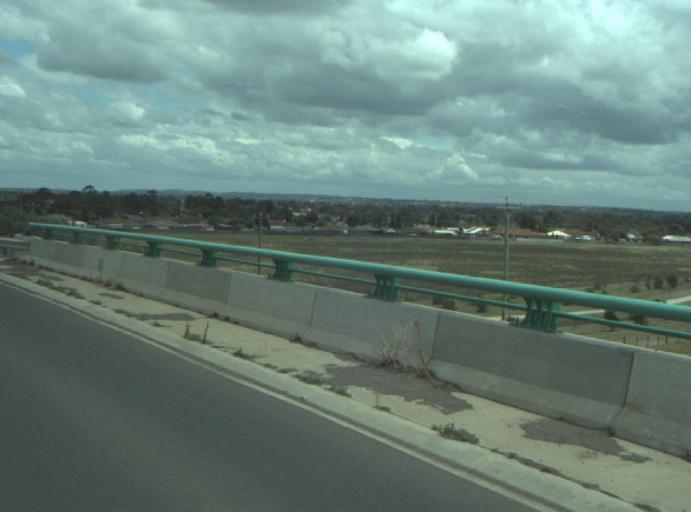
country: AU
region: Victoria
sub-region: Greater Geelong
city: Lara
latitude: -38.0591
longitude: 144.3783
